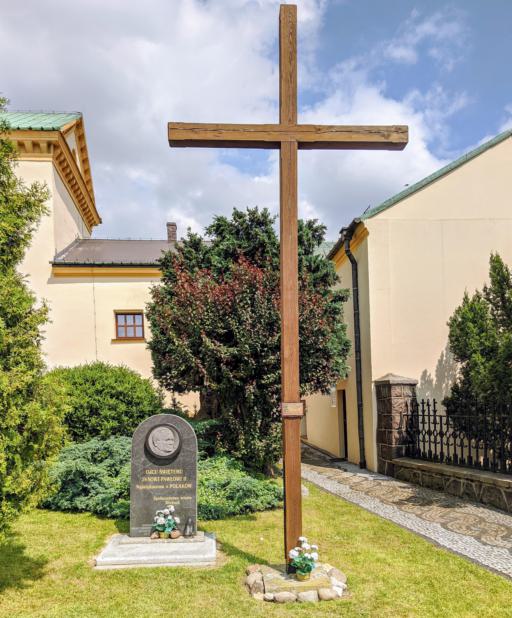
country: PL
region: Silesian Voivodeship
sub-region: Powiat klobucki
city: Klobuck
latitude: 50.9037
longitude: 18.9365
